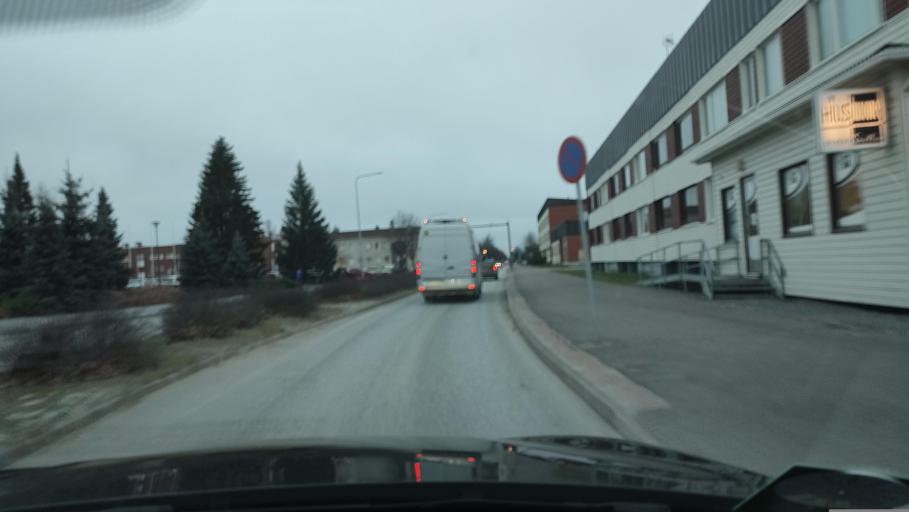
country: FI
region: Southern Ostrobothnia
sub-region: Suupohja
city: Kauhajoki
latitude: 62.4222
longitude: 22.1753
